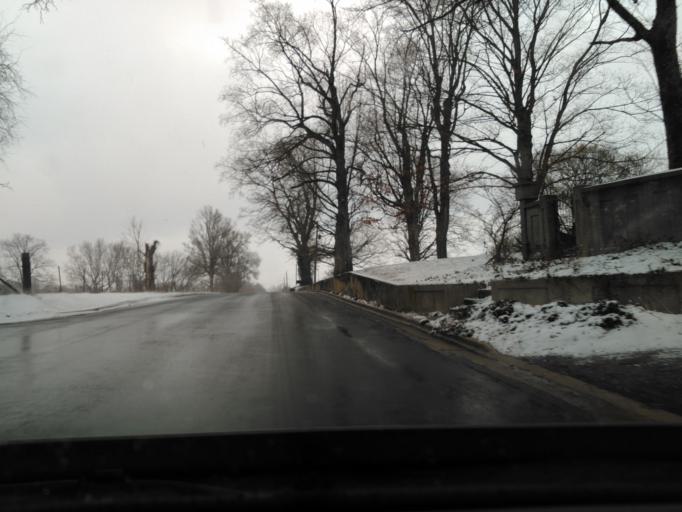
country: US
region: Illinois
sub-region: Bond County
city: Greenville
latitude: 38.8908
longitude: -89.3910
